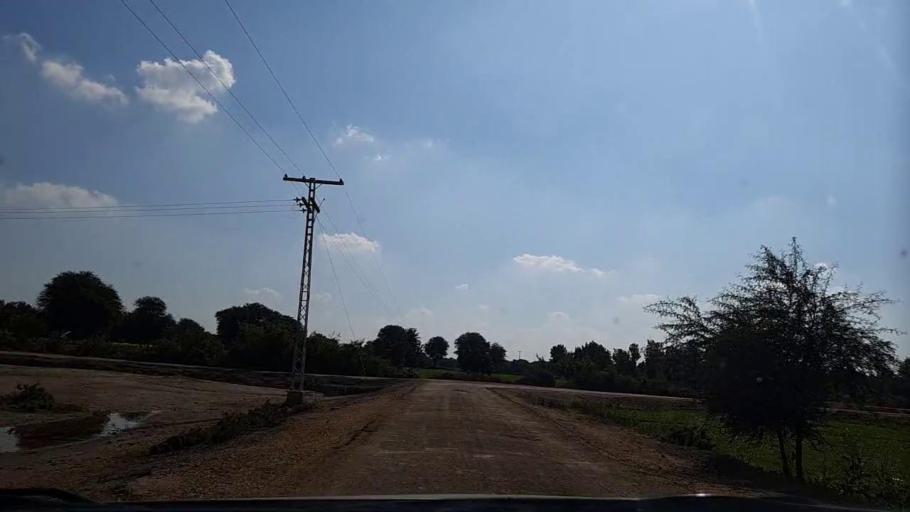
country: PK
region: Sindh
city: Pithoro
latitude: 25.6565
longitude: 69.4493
